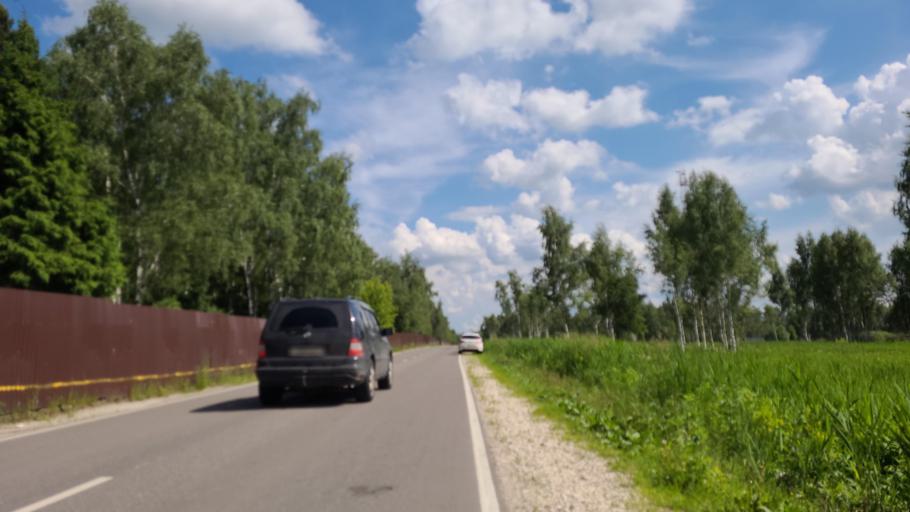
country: RU
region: Moskovskaya
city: Konobeyevo
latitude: 55.4013
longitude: 38.6760
